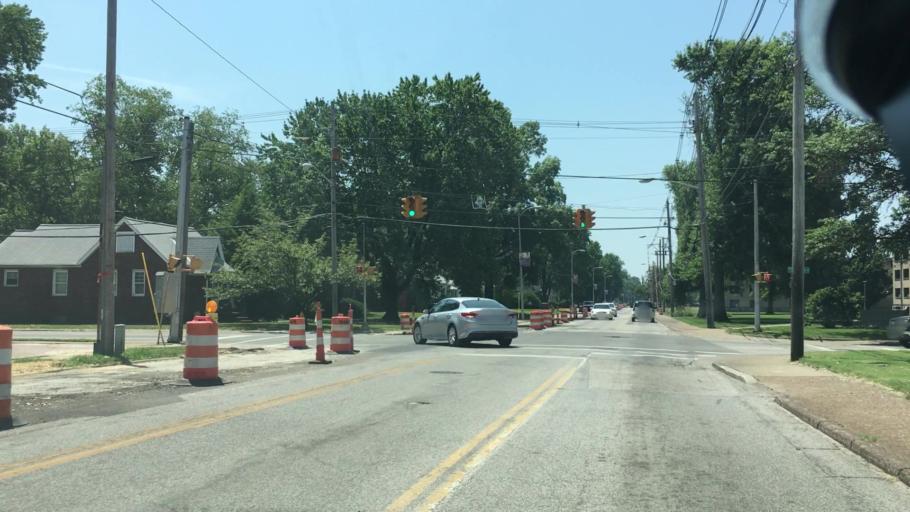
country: US
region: Indiana
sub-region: Vanderburgh County
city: Evansville
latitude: 37.9739
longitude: -87.5293
